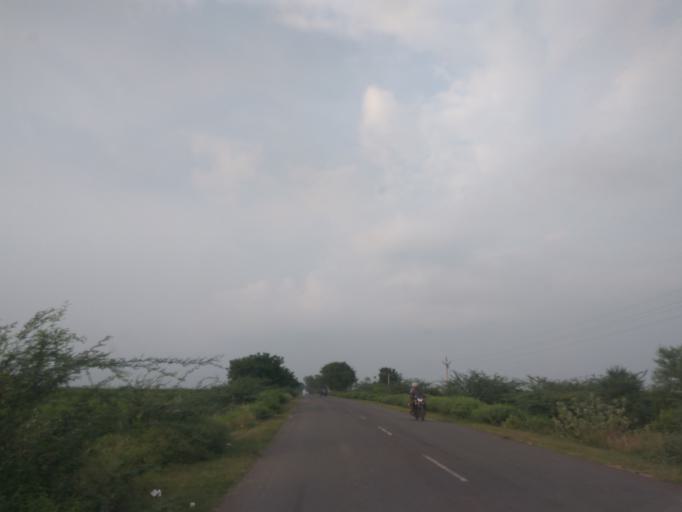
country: IN
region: Andhra Pradesh
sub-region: Guntur
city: Vinukonda
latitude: 16.0931
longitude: 79.7487
